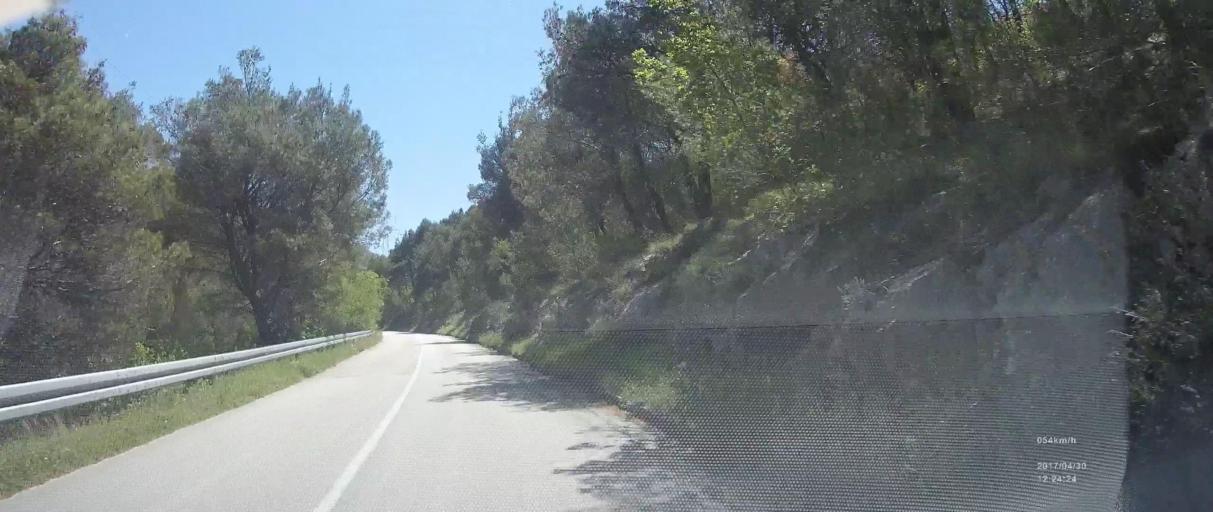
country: HR
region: Splitsko-Dalmatinska
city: Zrnovnica
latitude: 43.5118
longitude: 16.5854
